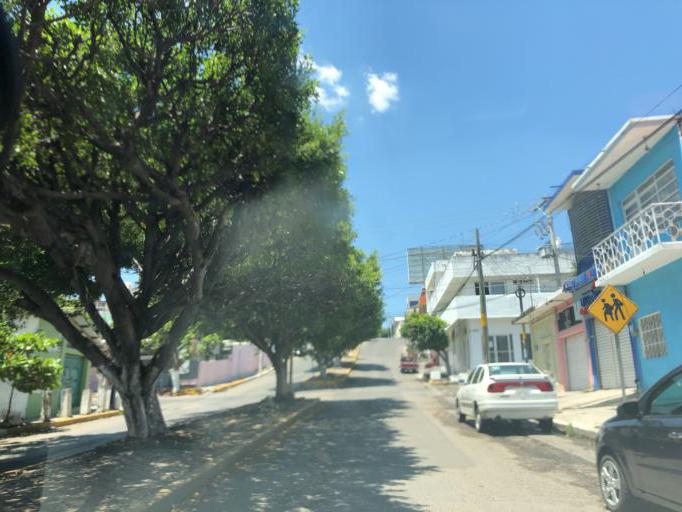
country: MX
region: Chiapas
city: Tuxtla Gutierrez
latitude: 16.7505
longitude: -93.1267
